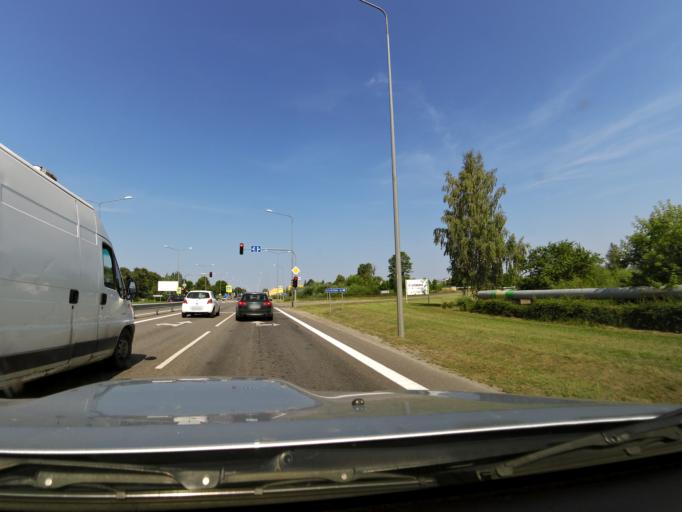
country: LT
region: Siauliu apskritis
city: Radviliskis
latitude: 55.8226
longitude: 23.5302
